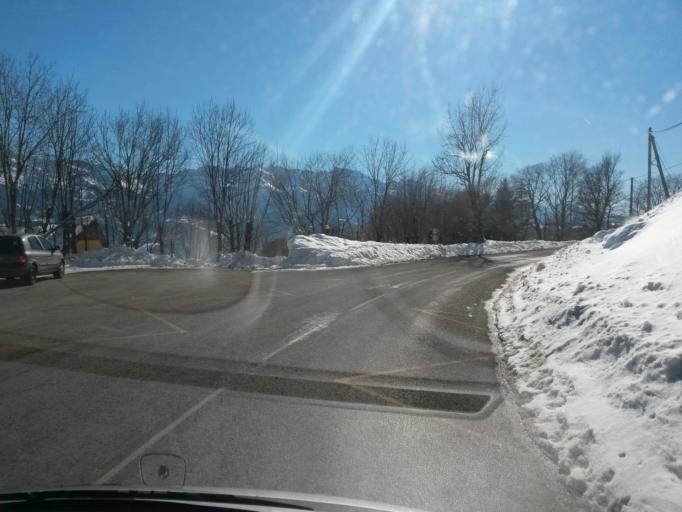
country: FR
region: Rhone-Alpes
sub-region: Departement de l'Isere
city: La Terrasse
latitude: 45.3424
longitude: 5.9053
